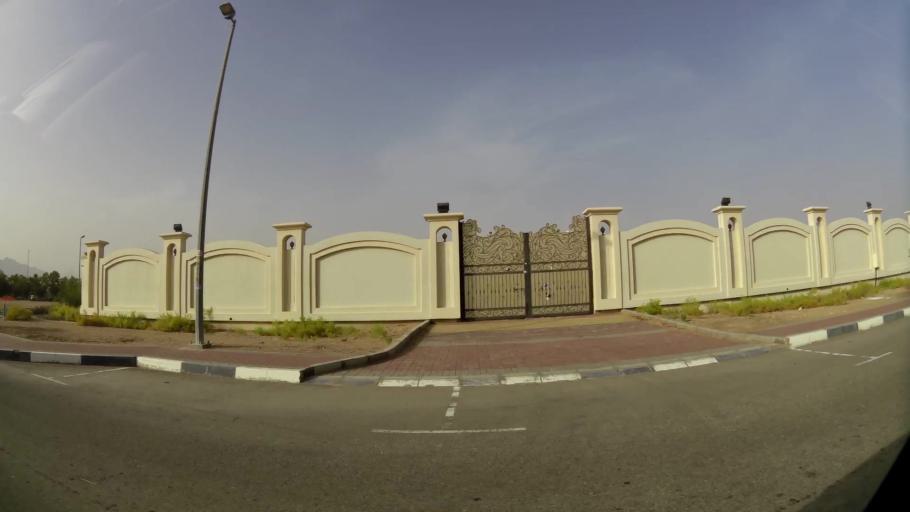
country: AE
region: Abu Dhabi
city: Al Ain
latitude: 24.1253
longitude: 55.7047
